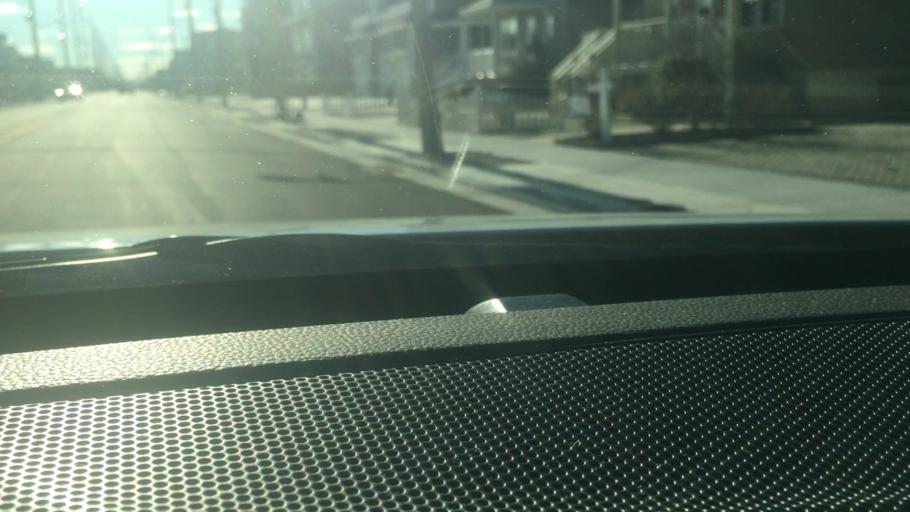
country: US
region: New Jersey
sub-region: Cape May County
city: Avalon
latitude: 39.0929
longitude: -74.7284
